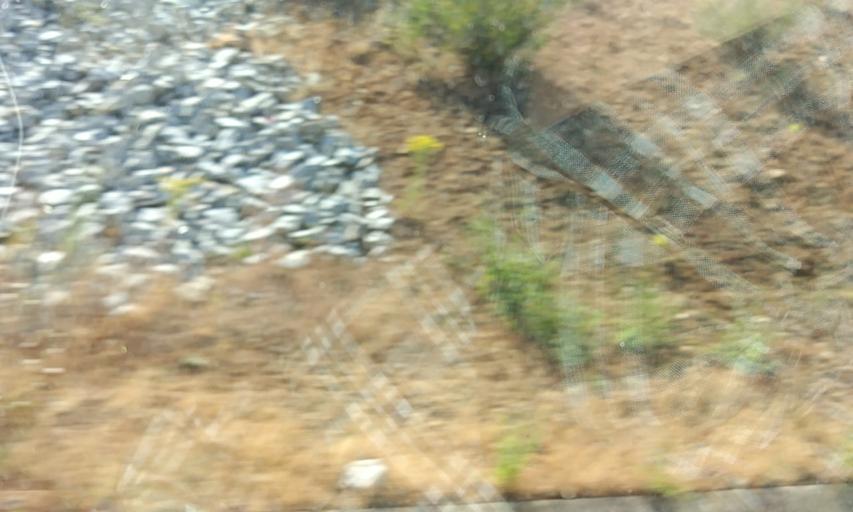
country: PT
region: Braganca
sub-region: Macedo de Cavaleiros
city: Macedo de Cavaleiros
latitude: 41.5699
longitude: -6.9814
